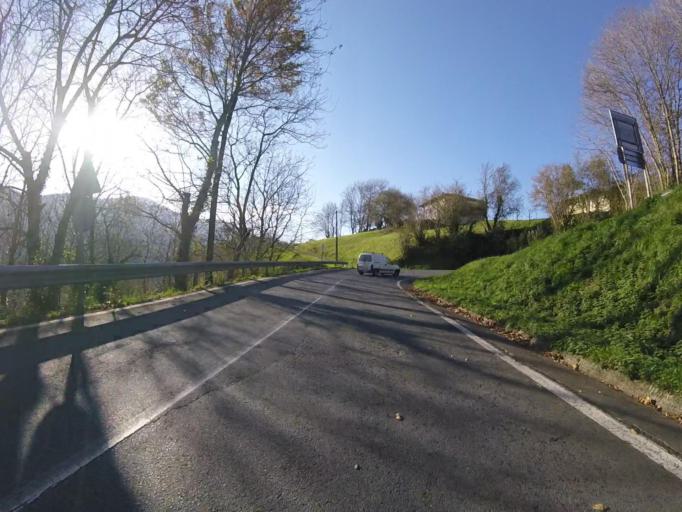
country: ES
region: Navarre
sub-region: Provincia de Navarra
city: Igantzi
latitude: 43.2226
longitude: -1.6966
